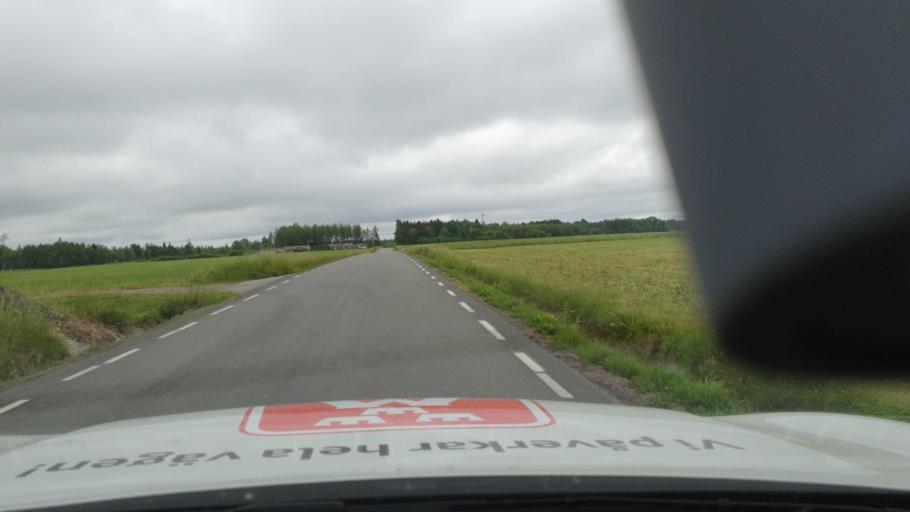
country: SE
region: Vaestra Goetaland
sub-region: Tibro Kommun
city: Tibro
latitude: 58.3825
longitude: 14.0548
